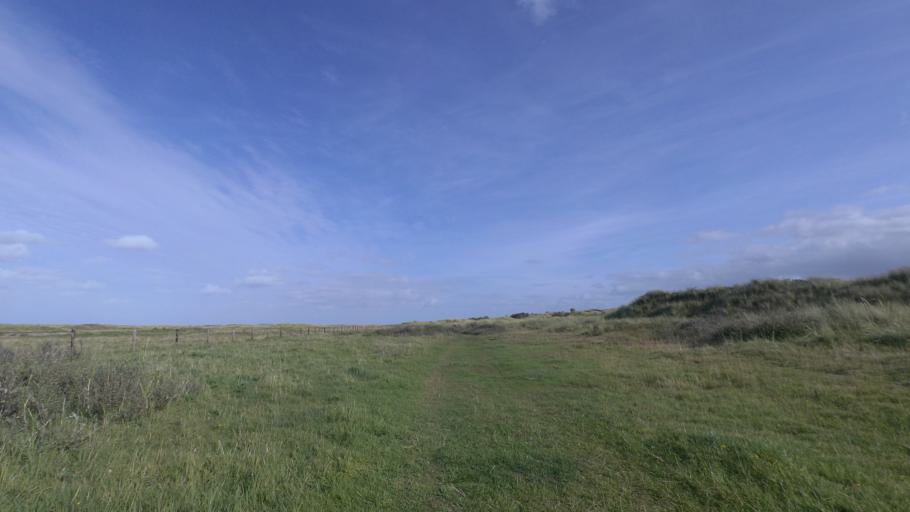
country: NL
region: Friesland
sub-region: Gemeente Ameland
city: Nes
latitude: 53.4531
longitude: 5.8426
